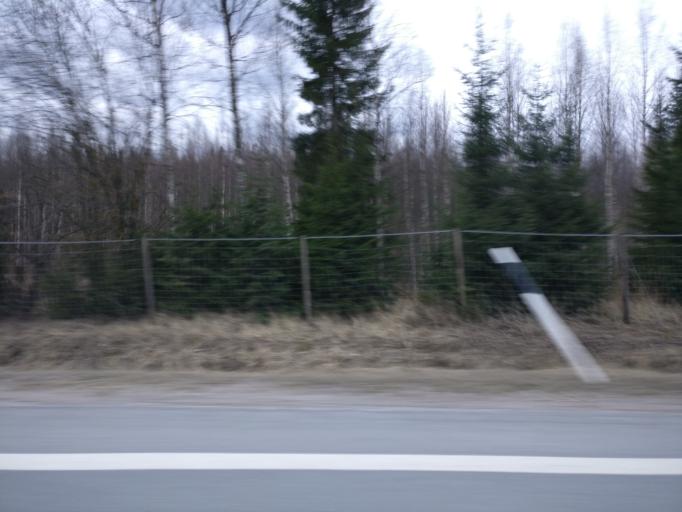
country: FI
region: Uusimaa
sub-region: Helsinki
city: Hyvinge
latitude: 60.6595
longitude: 24.7944
